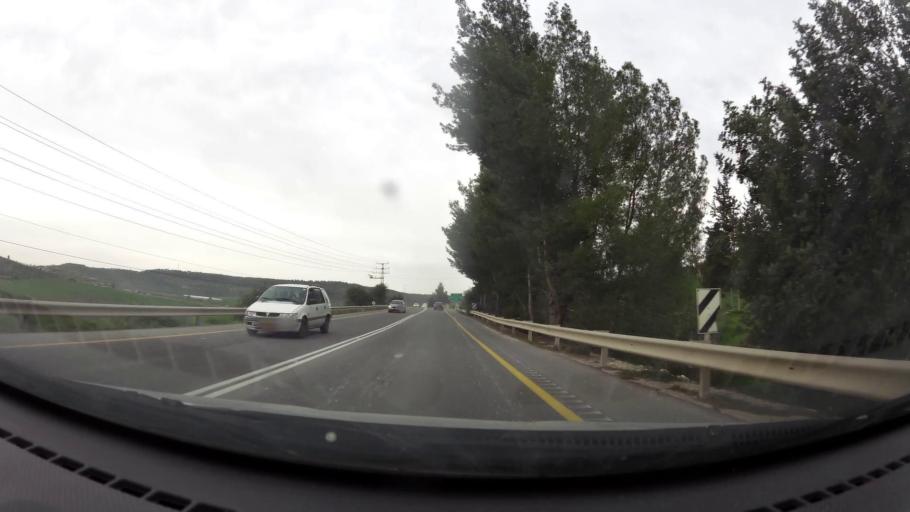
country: IL
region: Jerusalem
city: Bet Shemesh
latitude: 31.6864
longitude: 35.0010
